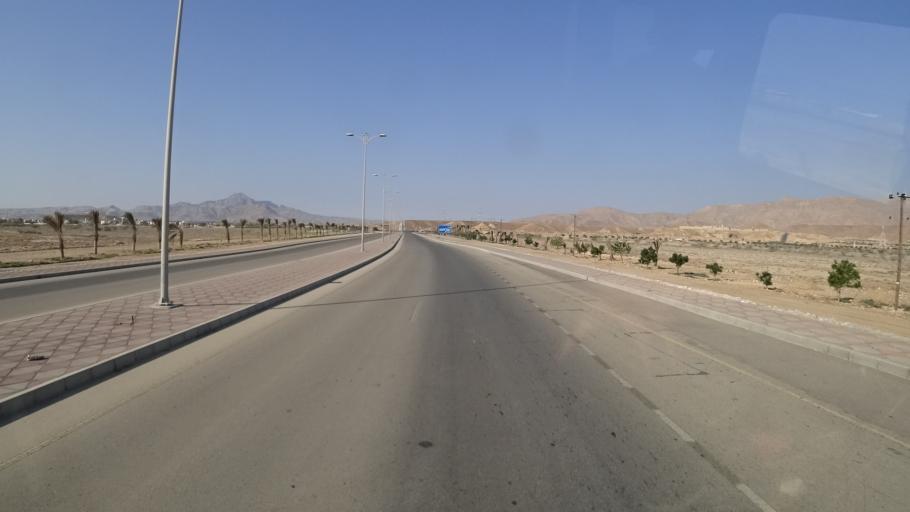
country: OM
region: Ash Sharqiyah
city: Sur
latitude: 22.5794
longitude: 59.4687
